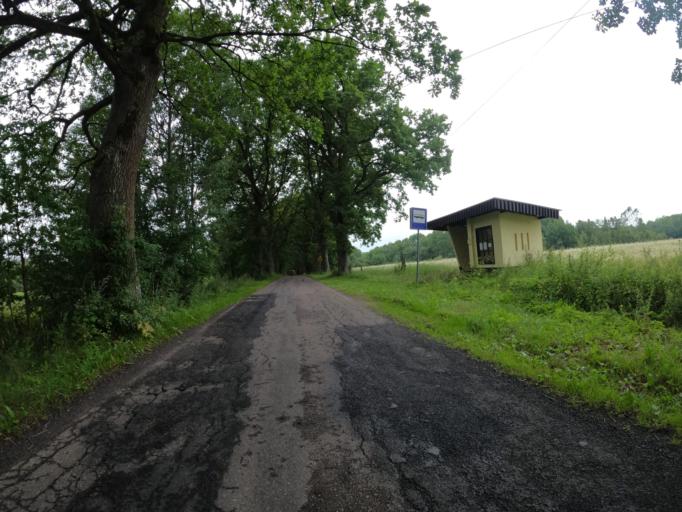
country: PL
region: West Pomeranian Voivodeship
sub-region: Powiat koszalinski
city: Bobolice
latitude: 53.9106
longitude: 16.5068
